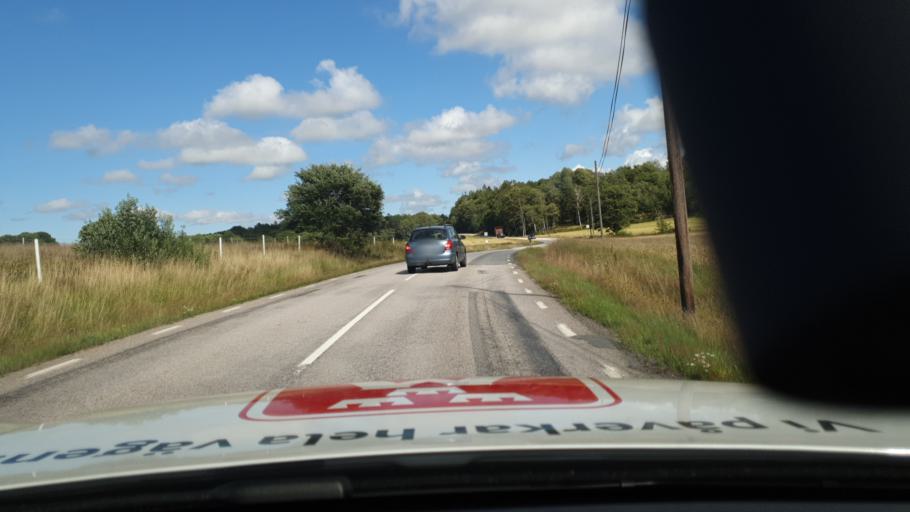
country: SE
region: Vaestra Goetaland
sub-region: Orust
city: Henan
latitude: 58.2237
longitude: 11.6162
